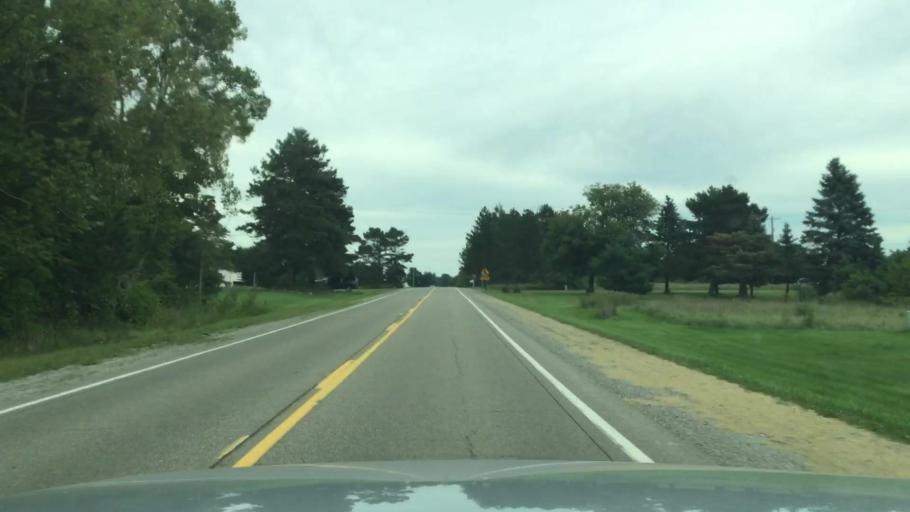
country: US
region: Michigan
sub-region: Shiawassee County
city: Durand
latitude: 42.9568
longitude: -83.9148
